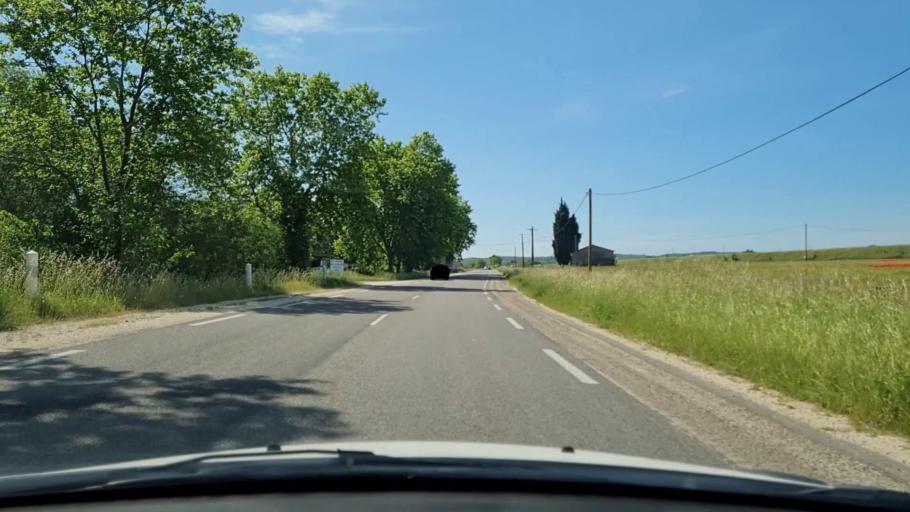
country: FR
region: Languedoc-Roussillon
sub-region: Departement du Gard
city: Saint-Genies-de-Malgoires
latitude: 43.9530
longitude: 4.2464
